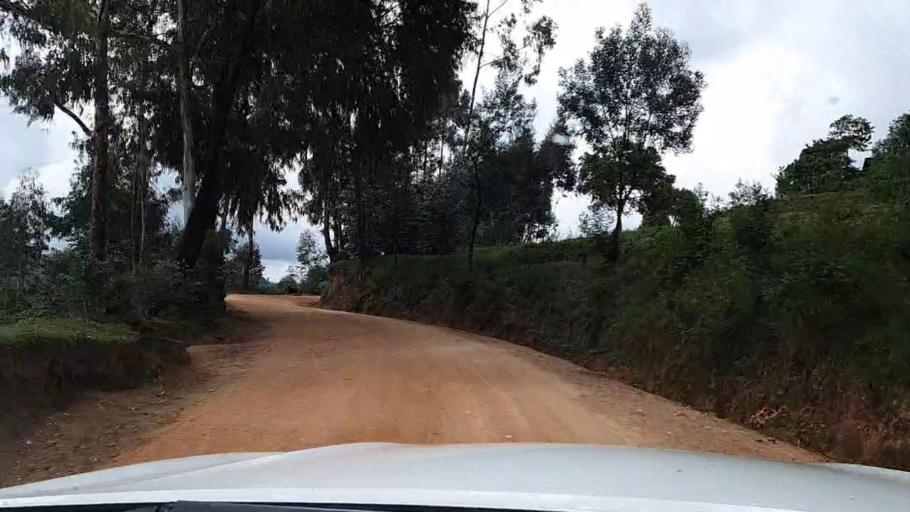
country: RW
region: Southern Province
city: Nzega
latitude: -2.4289
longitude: 29.4399
